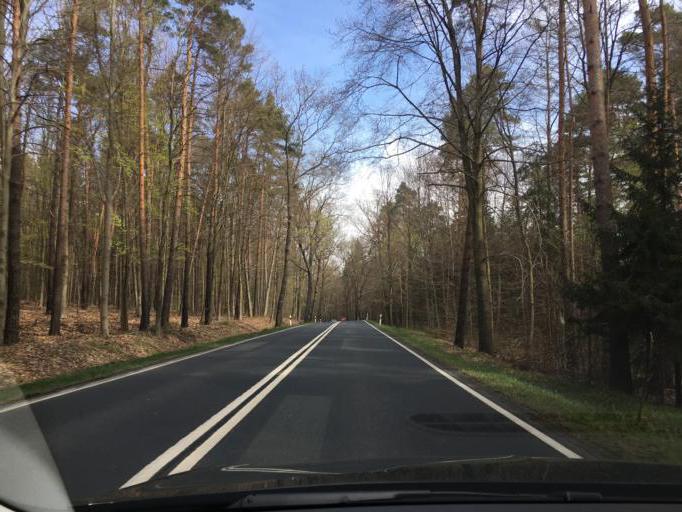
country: DE
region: Saxony
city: Ottendorf-Okrilla
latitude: 51.2227
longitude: 13.8432
